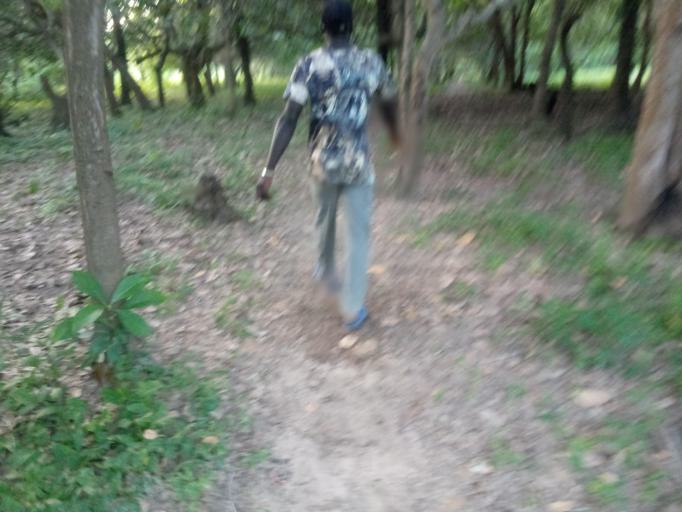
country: GM
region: Western
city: Gunjur
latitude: 13.0404
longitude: -16.7260
